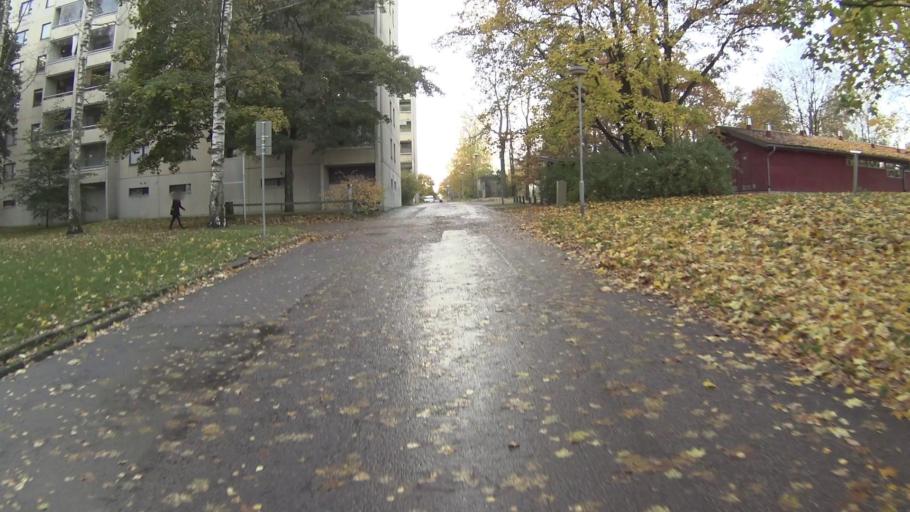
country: FI
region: Uusimaa
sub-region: Helsinki
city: Teekkarikylae
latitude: 60.2142
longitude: 24.8237
